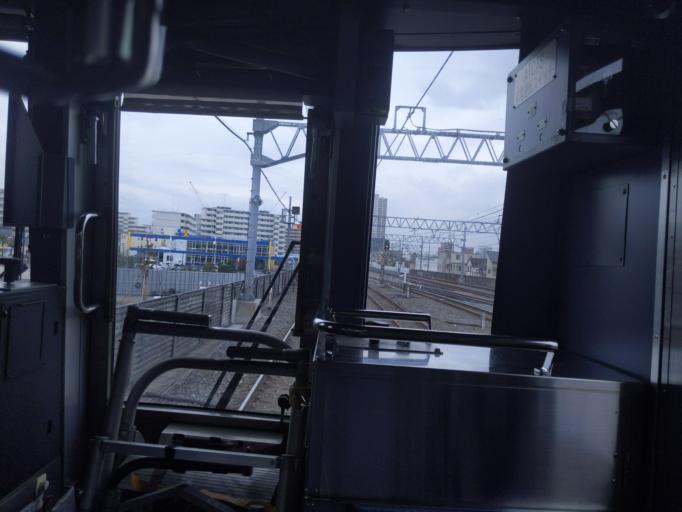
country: JP
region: Saitama
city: Soka
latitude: 35.7995
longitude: 139.7927
